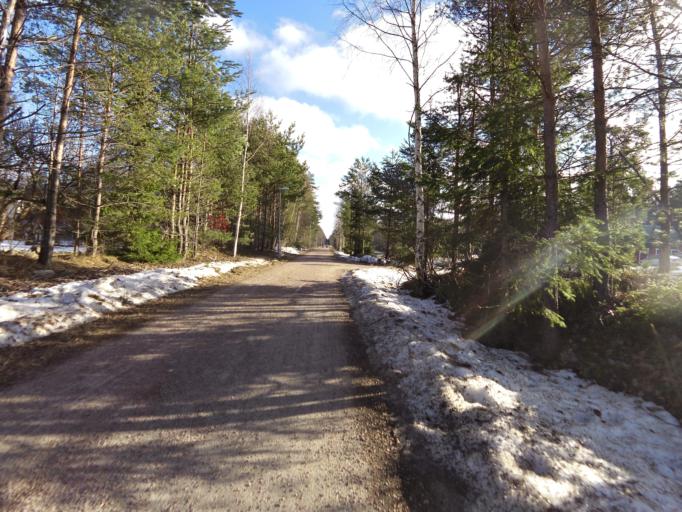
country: SE
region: Gaevleborg
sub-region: Gavle Kommun
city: Gavle
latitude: 60.6497
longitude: 17.2007
